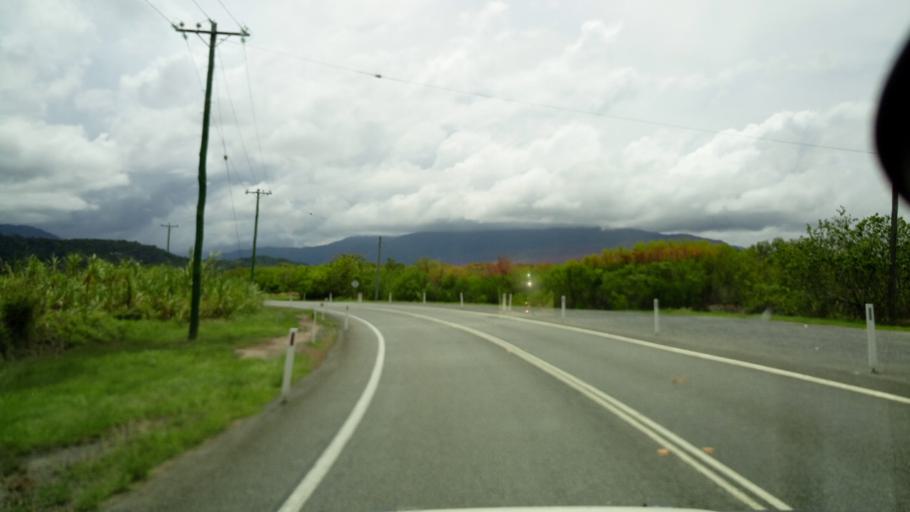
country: AU
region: Queensland
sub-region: Cairns
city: Redlynch
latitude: -16.8601
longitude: 145.7355
